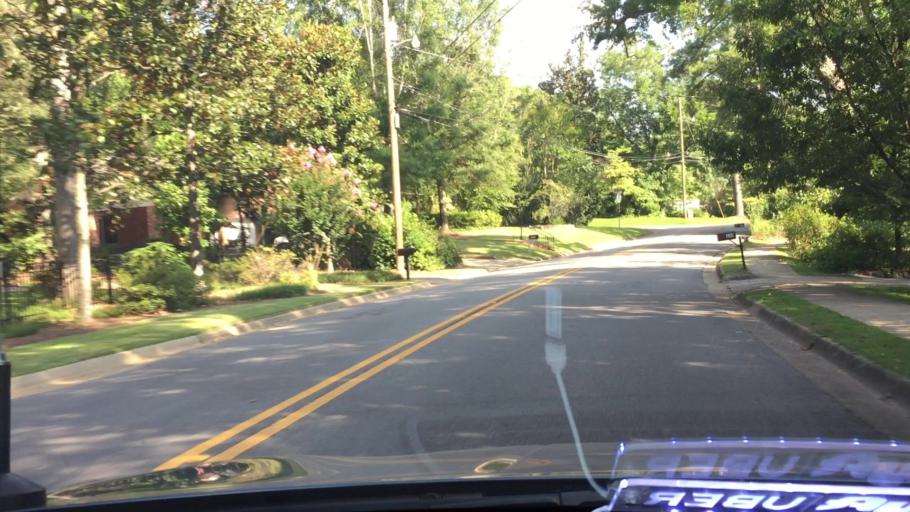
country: US
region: Alabama
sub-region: Lee County
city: Auburn
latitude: 32.6004
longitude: -85.4713
